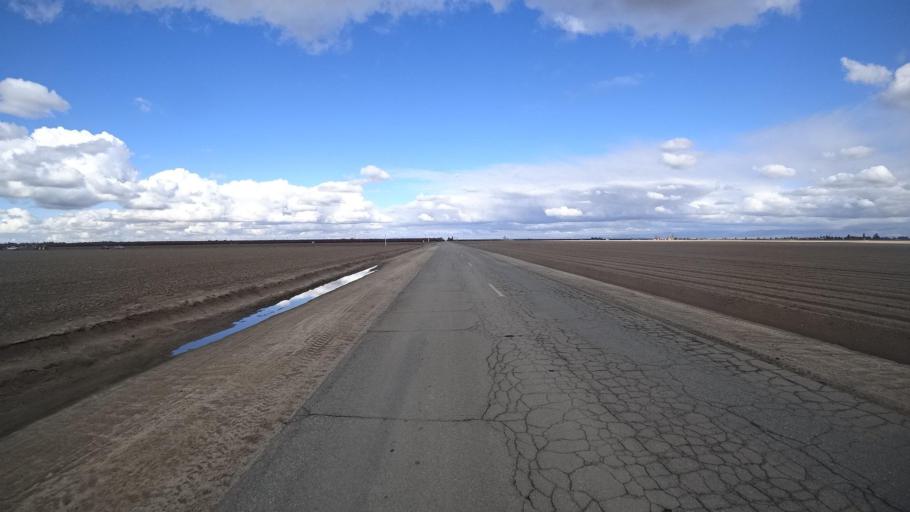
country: US
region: California
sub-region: Kern County
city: Greenfield
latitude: 35.2113
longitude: -119.0569
